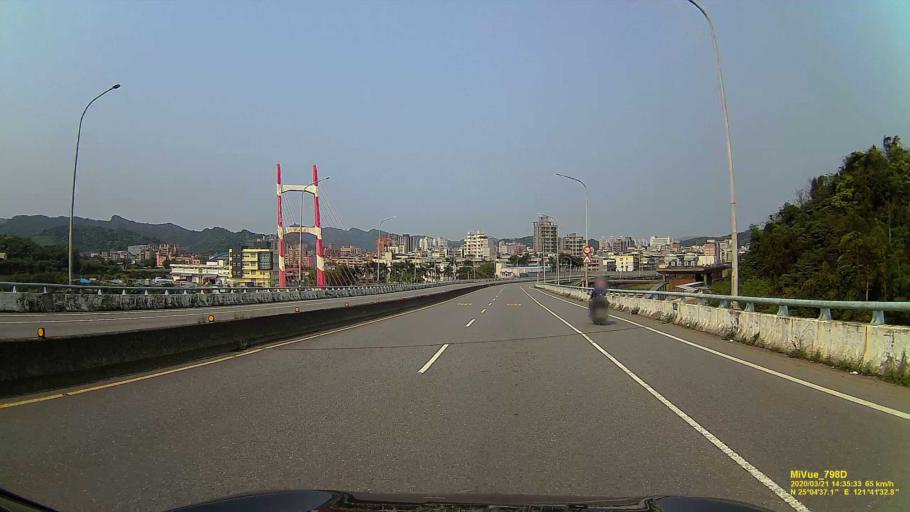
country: TW
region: Taiwan
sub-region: Keelung
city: Keelung
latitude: 25.0772
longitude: 121.6926
